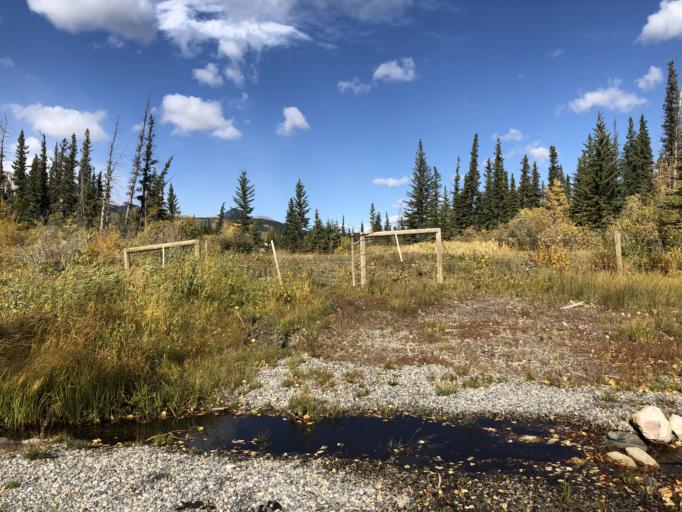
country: CA
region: Alberta
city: Canmore
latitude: 51.0984
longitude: -115.0614
